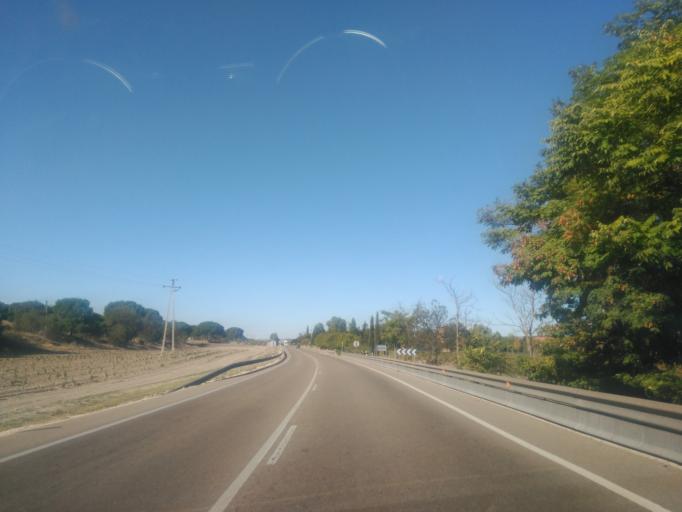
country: ES
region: Castille and Leon
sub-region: Provincia de Valladolid
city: Valbuena de Duero
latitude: 41.6286
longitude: -4.2894
